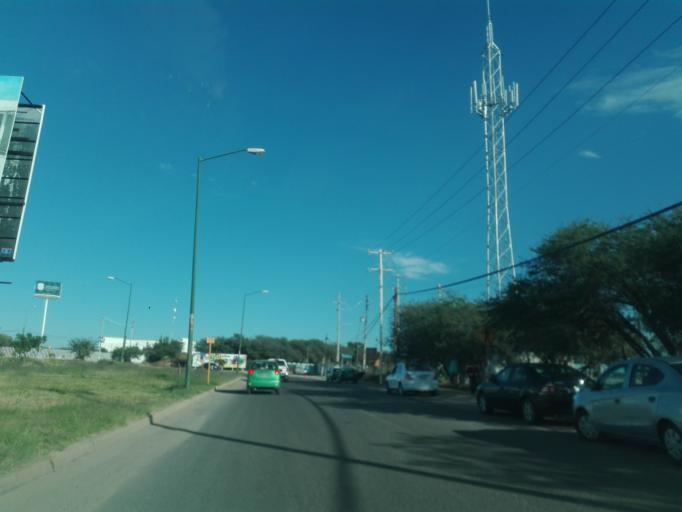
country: MX
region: Guanajuato
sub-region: Leon
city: Ladrilleras del Refugio
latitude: 21.0608
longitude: -101.5755
